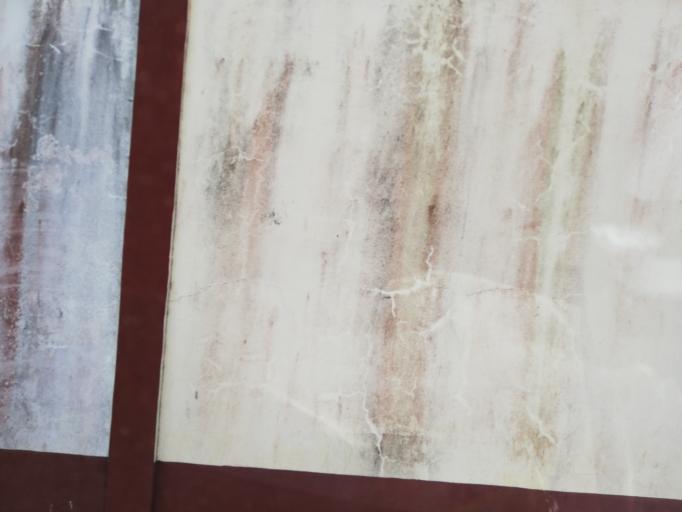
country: MU
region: Moka
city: Moka
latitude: -20.2191
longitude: 57.4747
